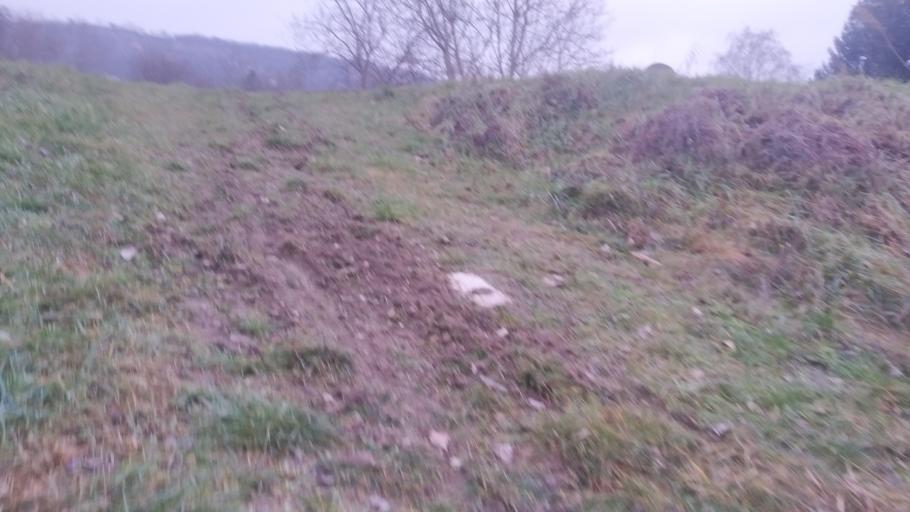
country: HU
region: Komarom-Esztergom
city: Dunaalmas
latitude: 47.7276
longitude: 18.3165
